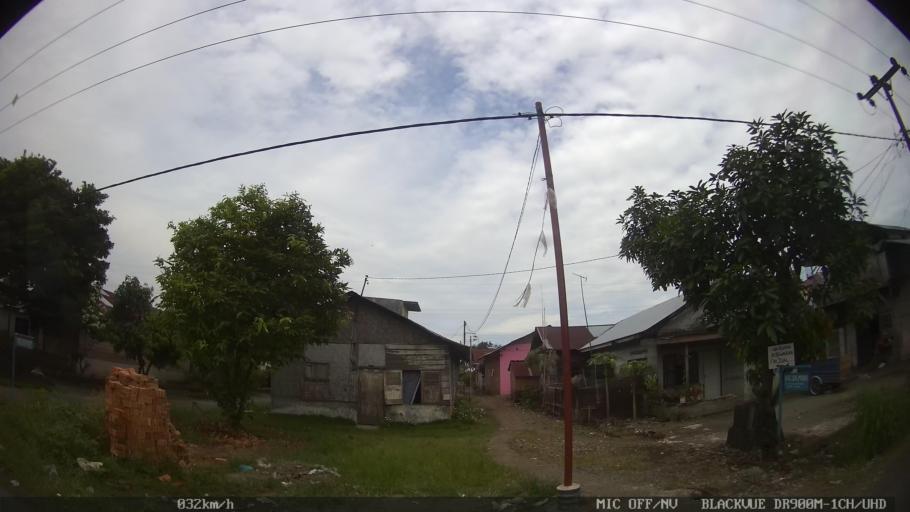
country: ID
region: North Sumatra
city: Sunggal
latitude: 3.6269
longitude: 98.5905
